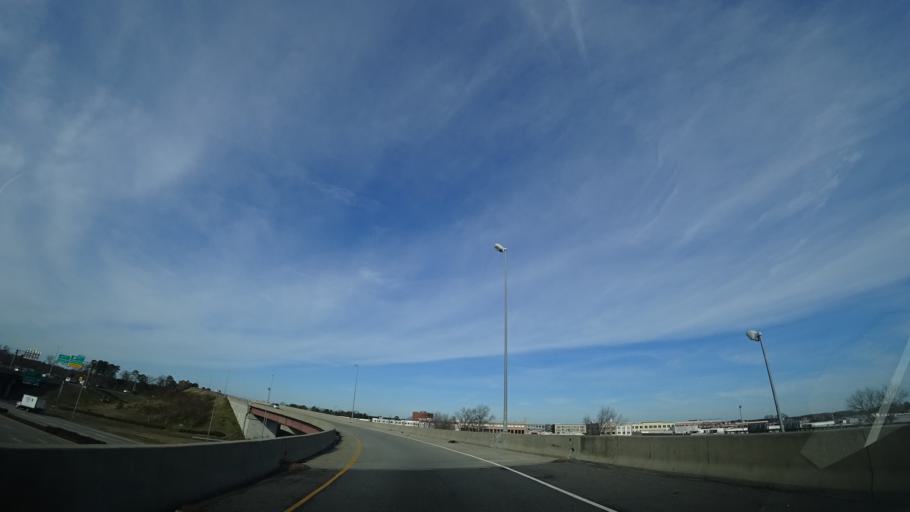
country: US
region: Virginia
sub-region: City of Hampton
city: Hampton
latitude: 37.0401
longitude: -76.3924
